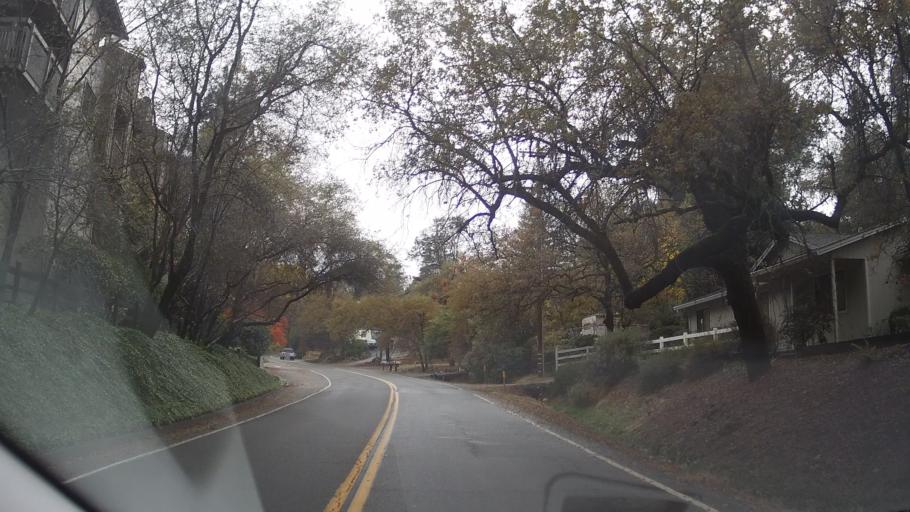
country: US
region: California
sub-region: Placer County
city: Auburn
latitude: 38.9144
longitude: -121.0750
